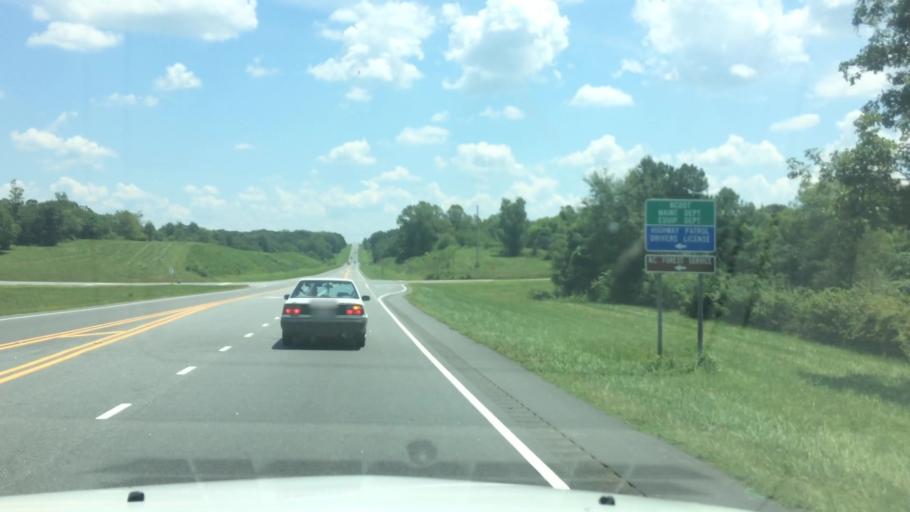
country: US
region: North Carolina
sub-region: Alexander County
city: Taylorsville
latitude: 35.9109
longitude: -81.1399
